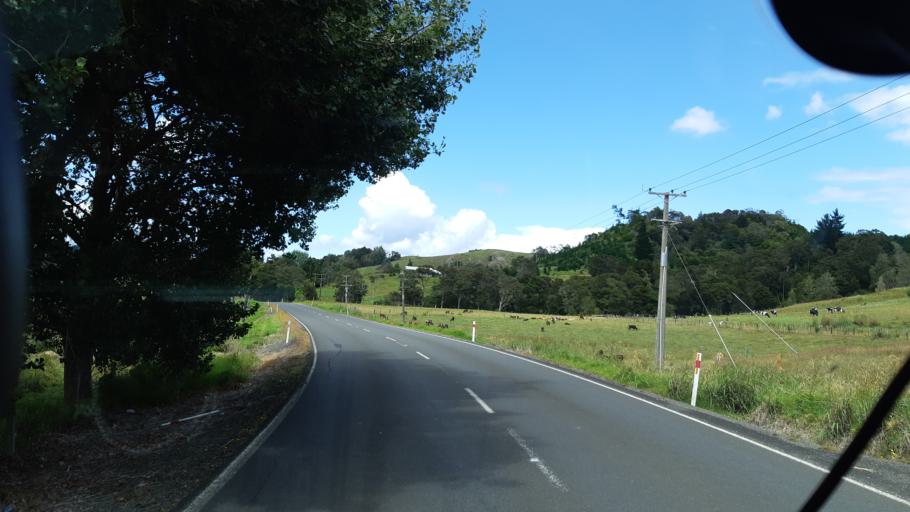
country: NZ
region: Northland
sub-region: Far North District
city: Taipa
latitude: -35.2582
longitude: 173.5291
